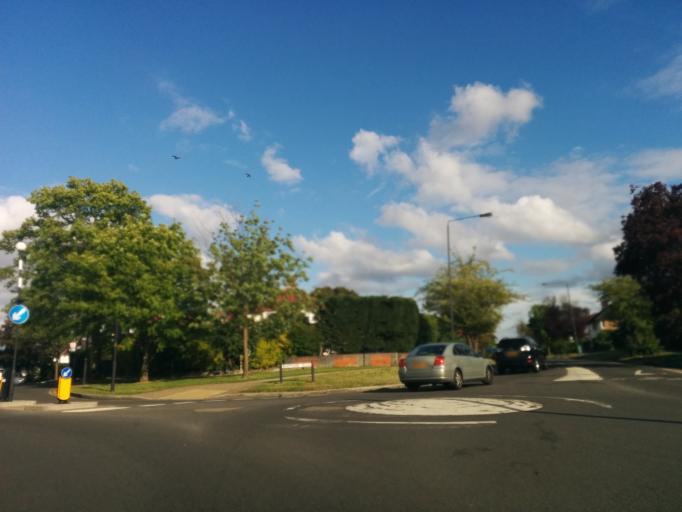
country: GB
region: England
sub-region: Greater London
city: Greenhill
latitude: 51.5753
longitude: -0.3575
